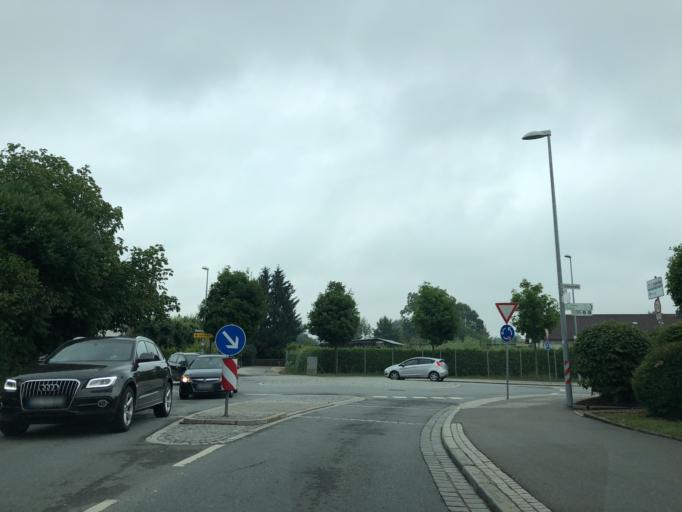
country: DE
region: Bavaria
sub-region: Upper Bavaria
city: Erding
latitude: 48.2942
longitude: 11.9104
